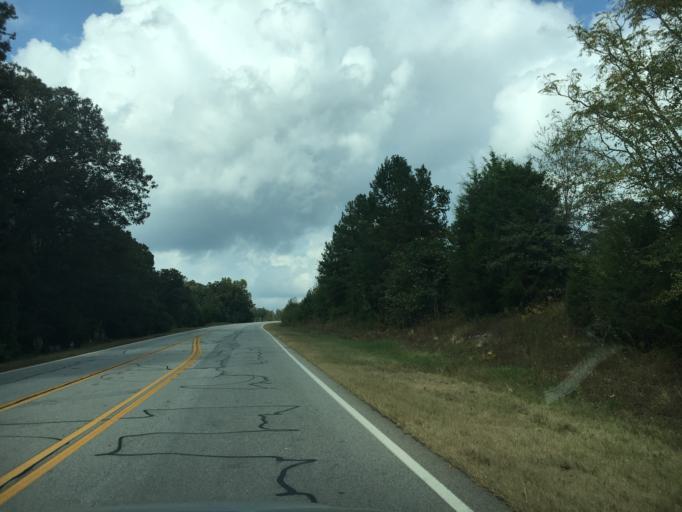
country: US
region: Georgia
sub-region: Elbert County
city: Elberton
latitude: 34.2224
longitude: -82.8941
